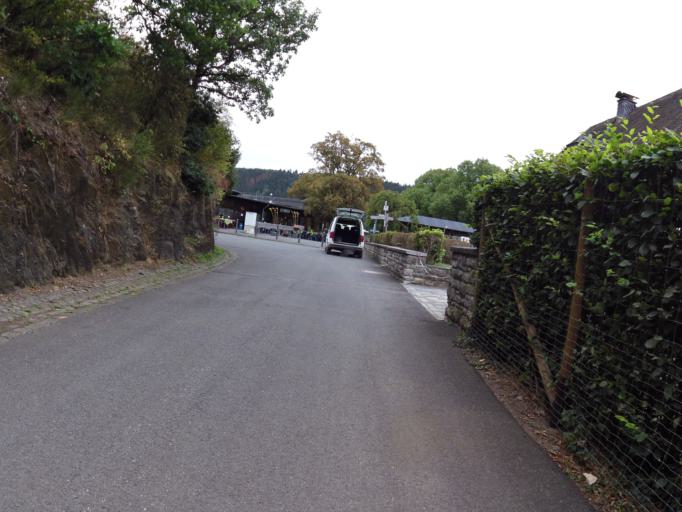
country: DE
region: North Rhine-Westphalia
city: Heimbach
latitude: 50.6045
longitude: 6.4203
